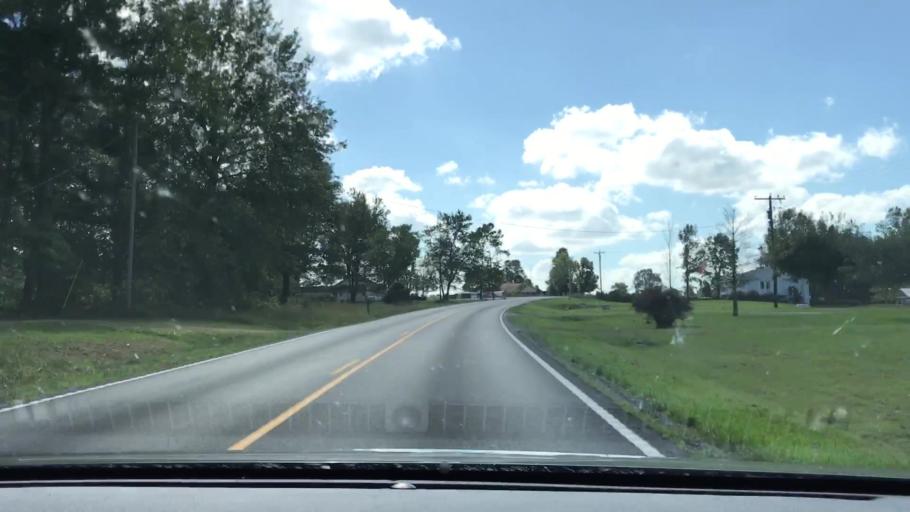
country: US
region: Kentucky
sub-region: Graves County
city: Mayfield
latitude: 36.8564
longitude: -88.5714
